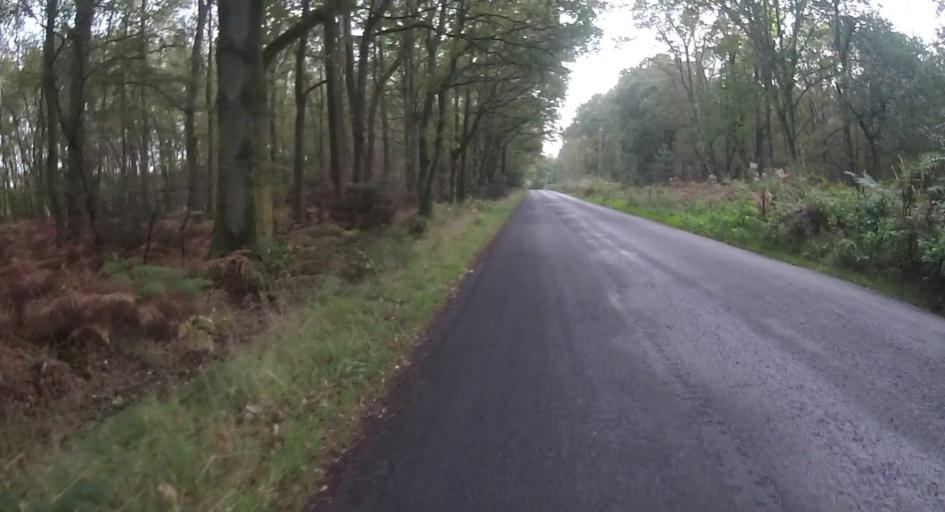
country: GB
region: England
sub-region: West Berkshire
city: Thatcham
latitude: 51.4166
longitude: -1.2013
